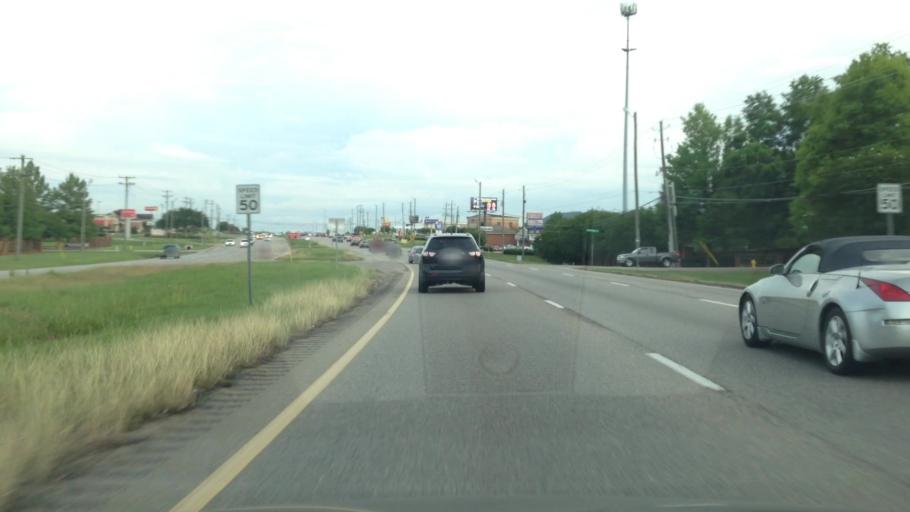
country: US
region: Alabama
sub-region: Montgomery County
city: Pike Road
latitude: 32.3436
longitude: -86.1794
